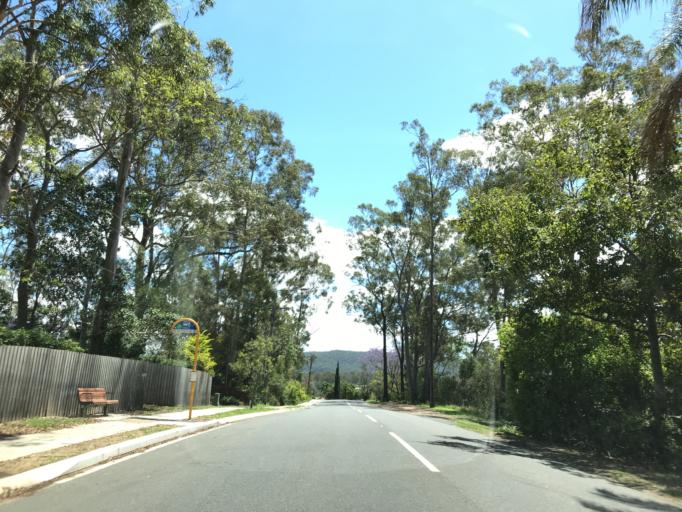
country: AU
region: Queensland
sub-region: Brisbane
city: Seventeen Mile Rocks
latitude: -27.5225
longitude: 152.9566
